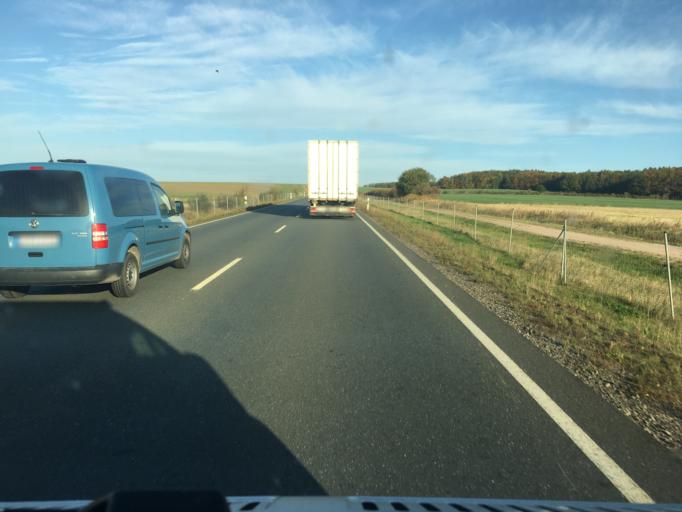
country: DE
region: Saxony
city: Lichtentanne
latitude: 50.7188
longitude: 12.4193
